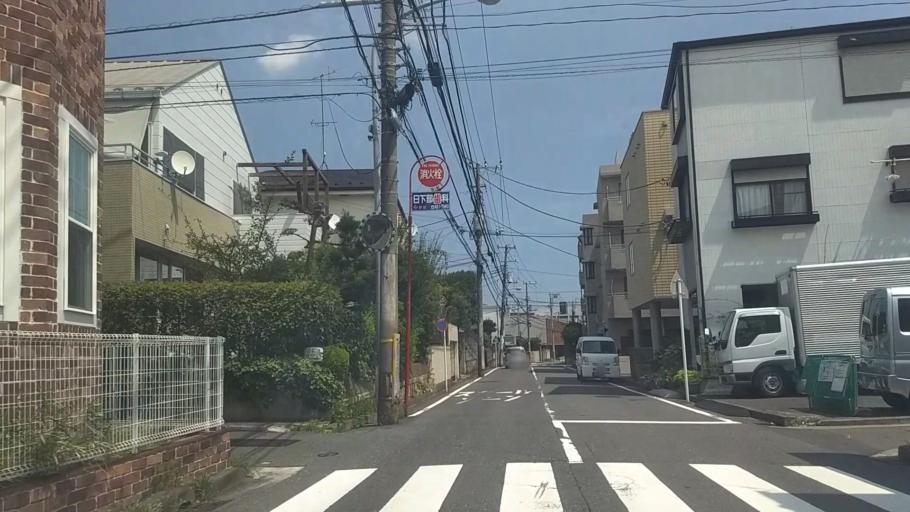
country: JP
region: Kanagawa
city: Yokohama
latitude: 35.4871
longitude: 139.6202
